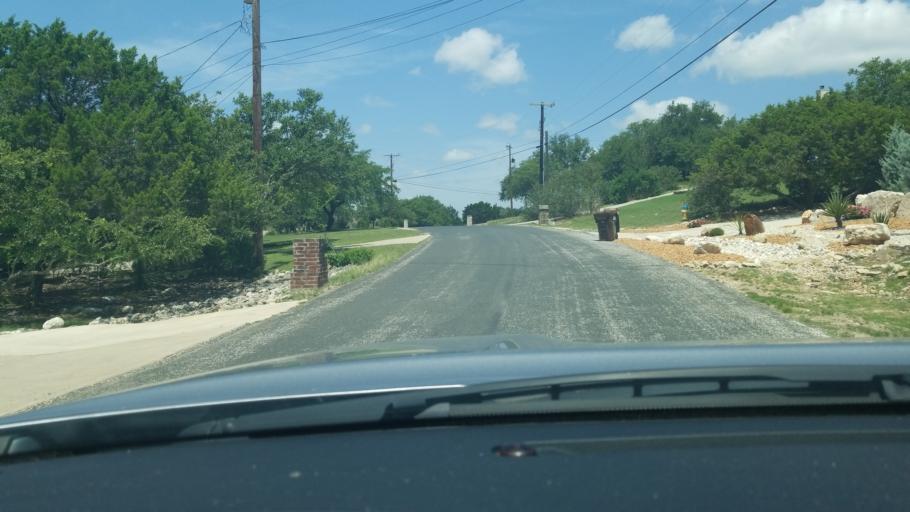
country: US
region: Texas
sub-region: Bexar County
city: Timberwood Park
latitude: 29.6920
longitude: -98.4853
